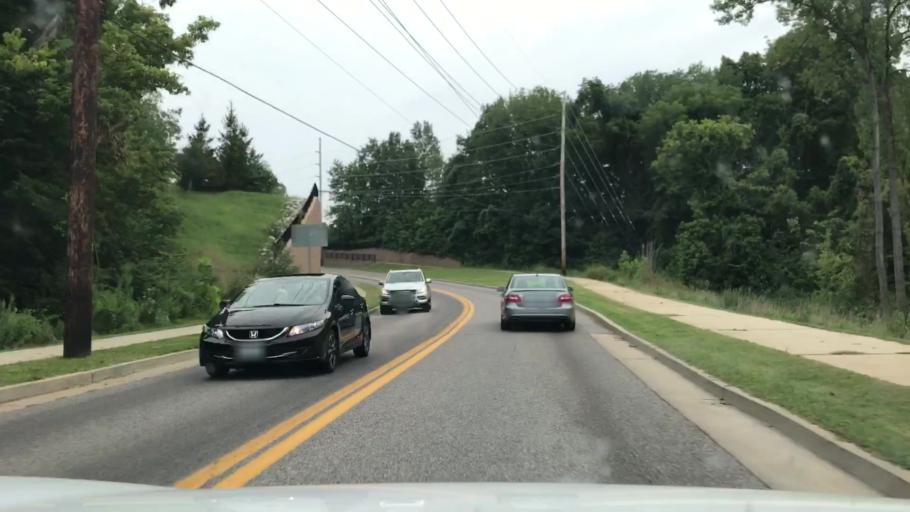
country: US
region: Missouri
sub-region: Saint Louis County
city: Chesterfield
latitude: 38.6564
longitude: -90.6185
